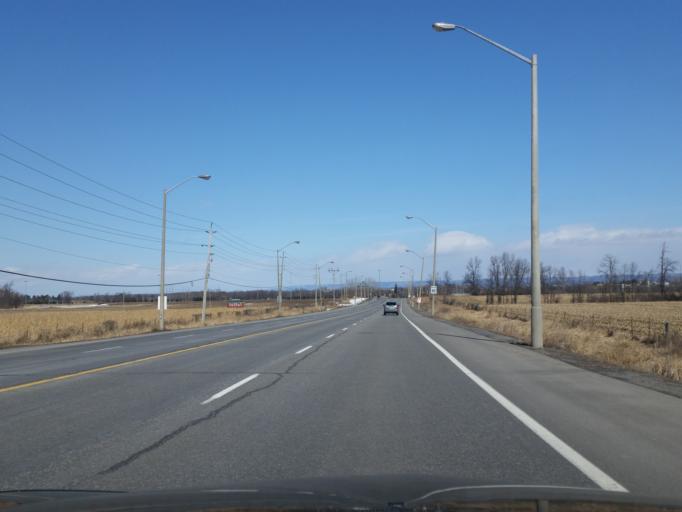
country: CA
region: Ontario
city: Bells Corners
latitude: 45.3303
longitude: -75.8379
